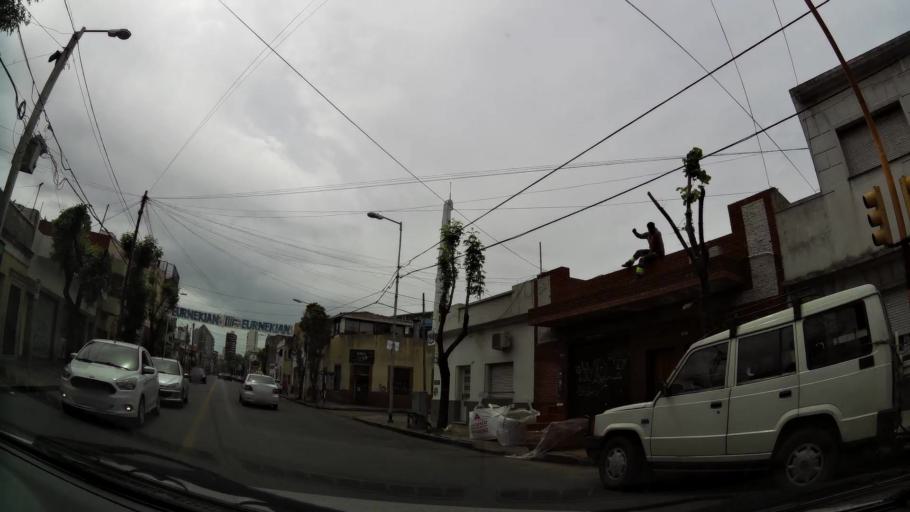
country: AR
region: Buenos Aires
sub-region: Partido de Avellaneda
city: Avellaneda
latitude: -34.6677
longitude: -58.3709
